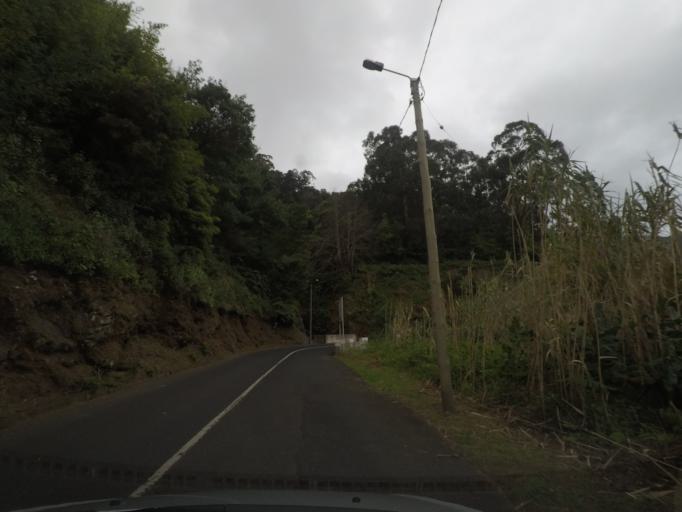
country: PT
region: Madeira
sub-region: Santana
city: Santana
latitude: 32.7530
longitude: -16.8377
